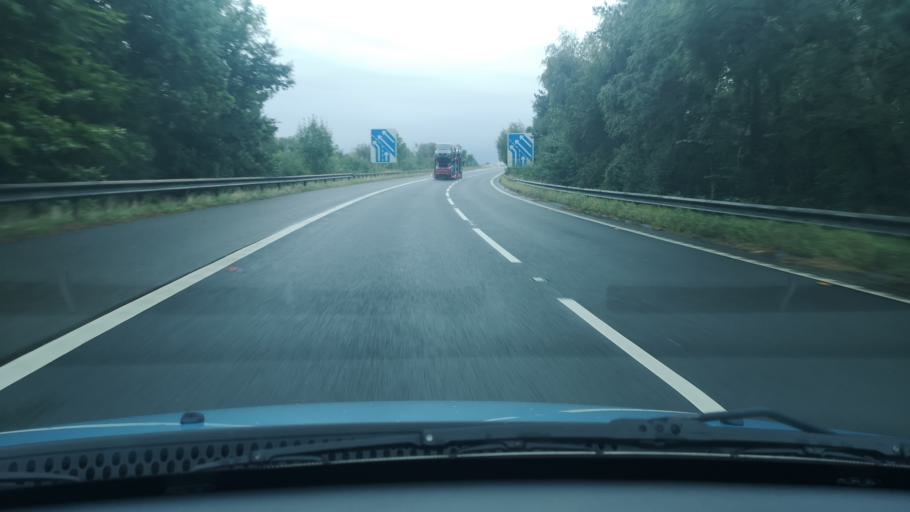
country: GB
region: England
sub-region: East Riding of Yorkshire
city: Rawcliffe
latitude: 53.6823
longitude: -0.9674
